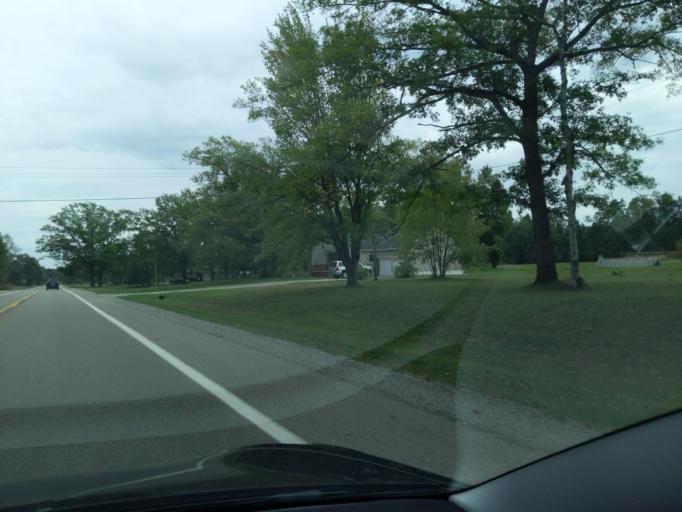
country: US
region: Michigan
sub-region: Clare County
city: Clare
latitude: 43.8467
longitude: -84.8896
